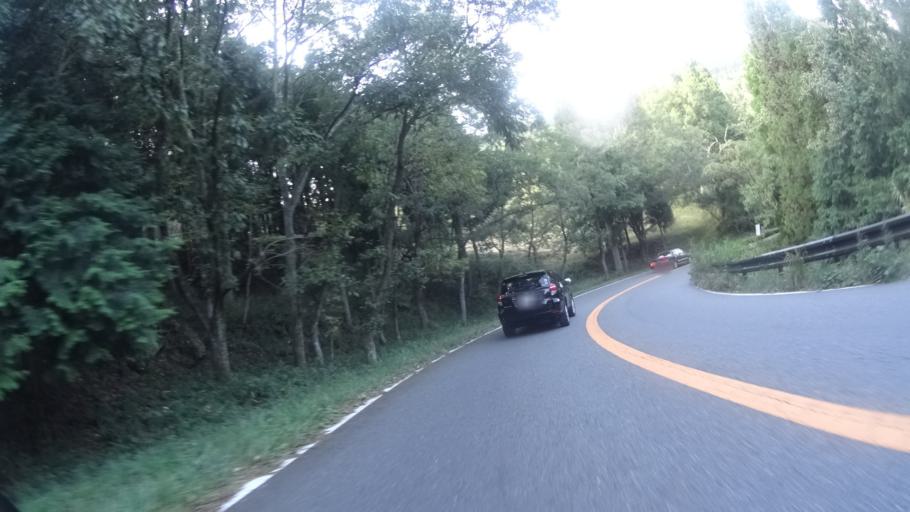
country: JP
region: Oita
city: Beppu
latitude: 33.2691
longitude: 131.4320
